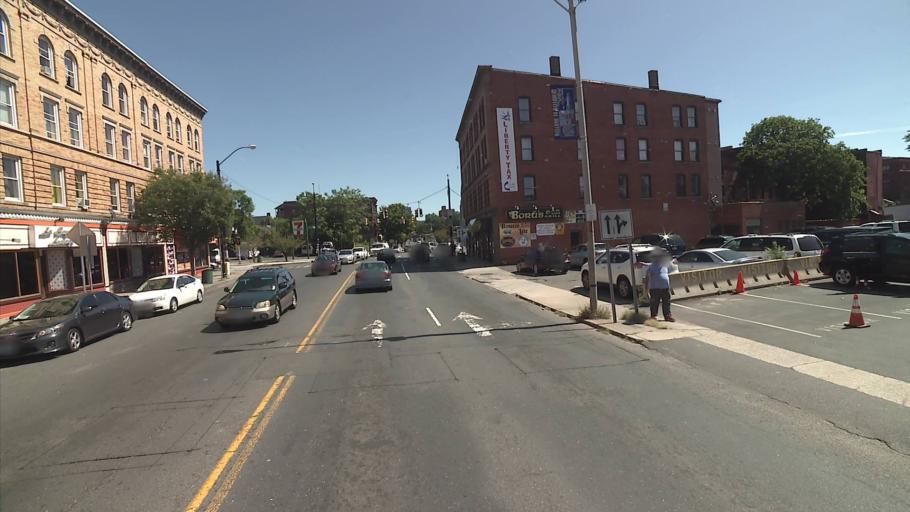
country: US
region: Connecticut
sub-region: New Haven County
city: Waterbury
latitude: 41.5579
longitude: -73.0473
